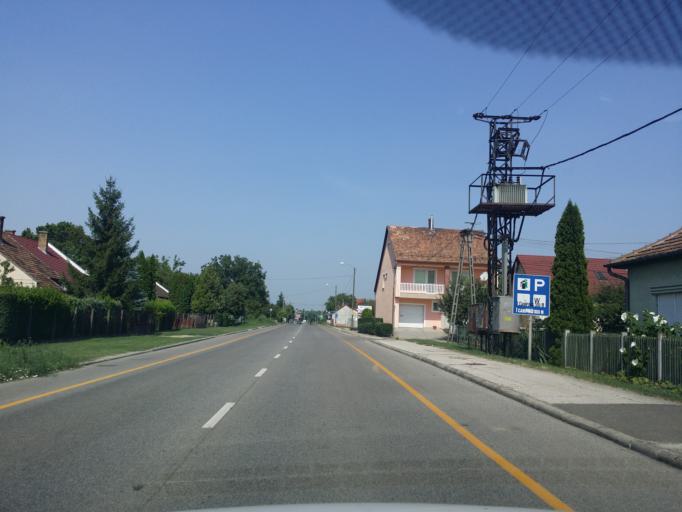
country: HU
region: Tolna
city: Simontornya
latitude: 46.7551
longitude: 18.5402
